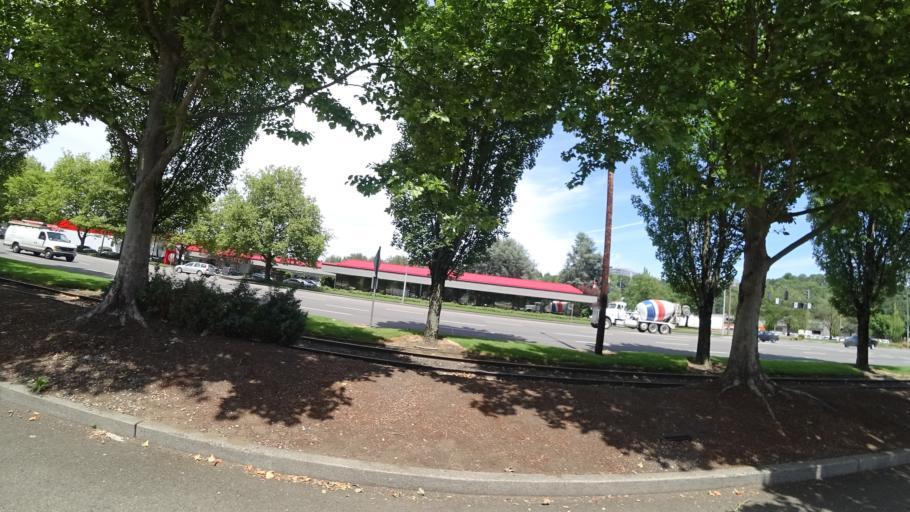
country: US
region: Oregon
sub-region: Multnomah County
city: Portland
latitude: 45.5559
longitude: -122.6991
